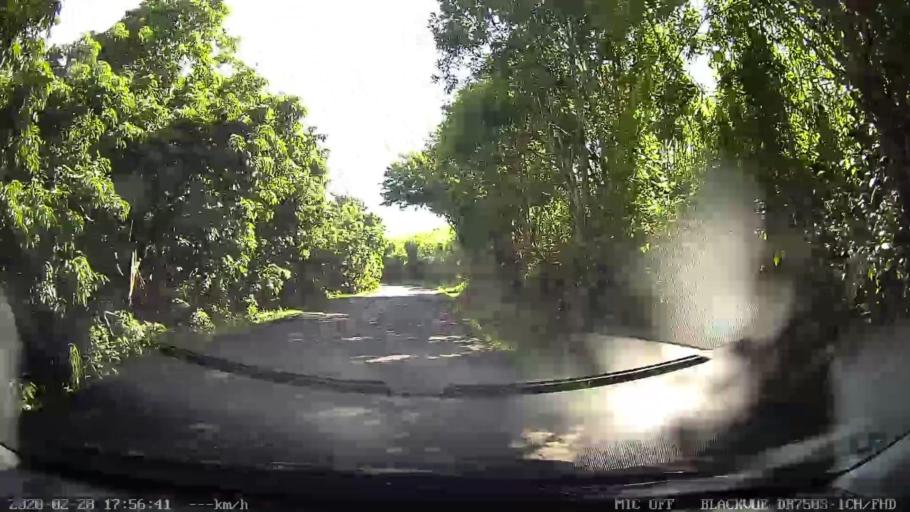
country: RE
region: Reunion
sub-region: Reunion
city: Sainte-Marie
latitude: -20.9386
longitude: 55.5250
